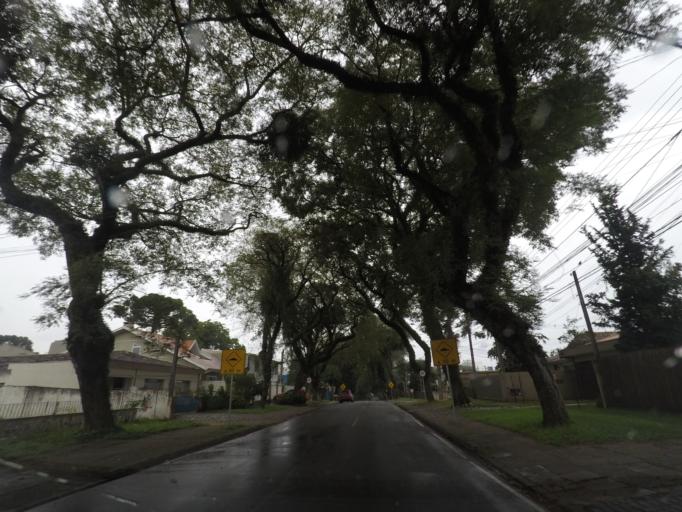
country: BR
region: Parana
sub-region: Curitiba
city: Curitiba
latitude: -25.4758
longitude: -49.3006
